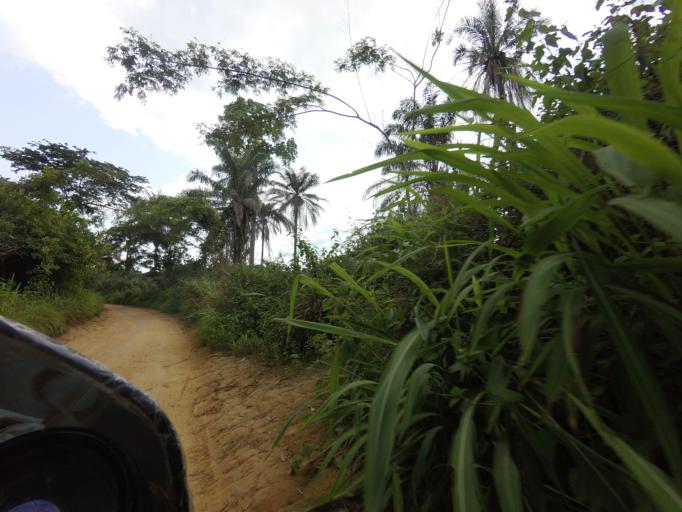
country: SL
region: Eastern Province
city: Manowa
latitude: 8.1500
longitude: -10.7693
